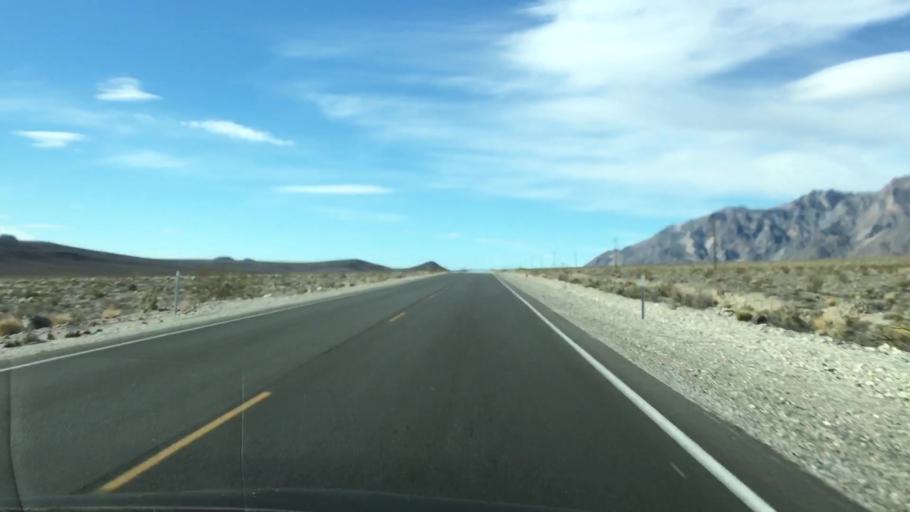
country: US
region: Nevada
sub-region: Nye County
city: Pahrump
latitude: 36.3250
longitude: -116.5632
